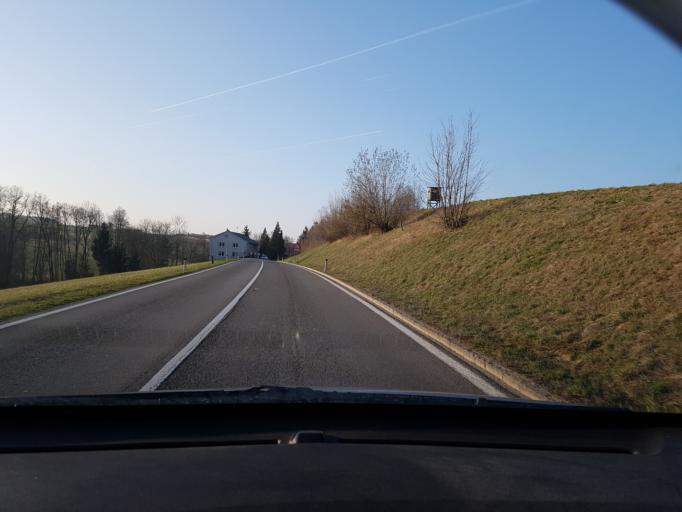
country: AT
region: Upper Austria
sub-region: Politischer Bezirk Linz-Land
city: Ansfelden
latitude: 48.1410
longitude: 14.3270
